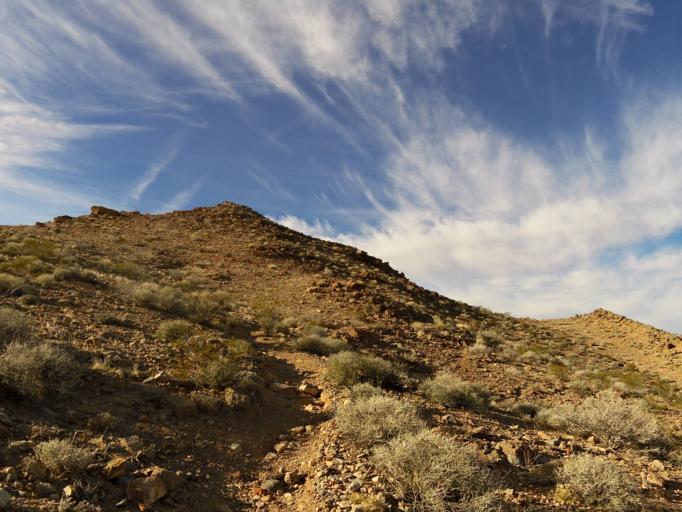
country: US
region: Nevada
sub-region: Clark County
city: Boulder City
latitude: 36.2285
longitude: -114.6231
